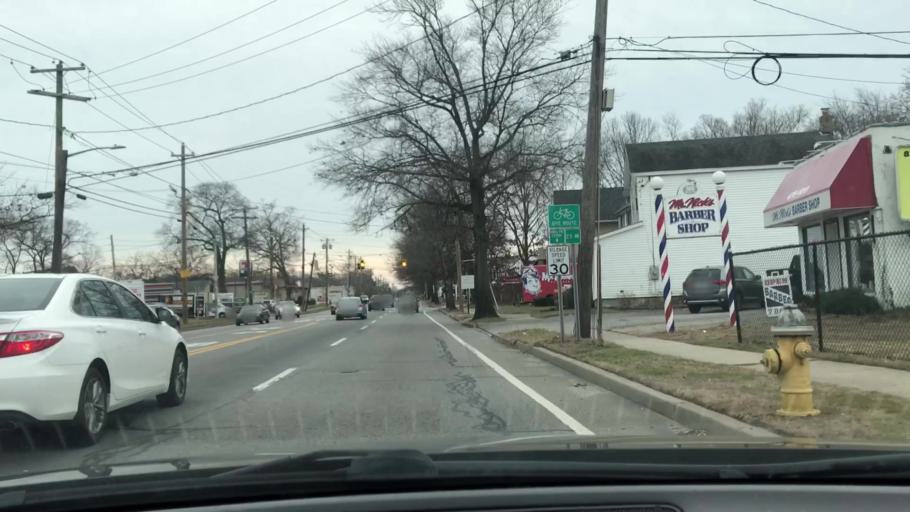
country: US
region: New York
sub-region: Suffolk County
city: Patchogue
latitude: 40.7753
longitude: -73.0287
